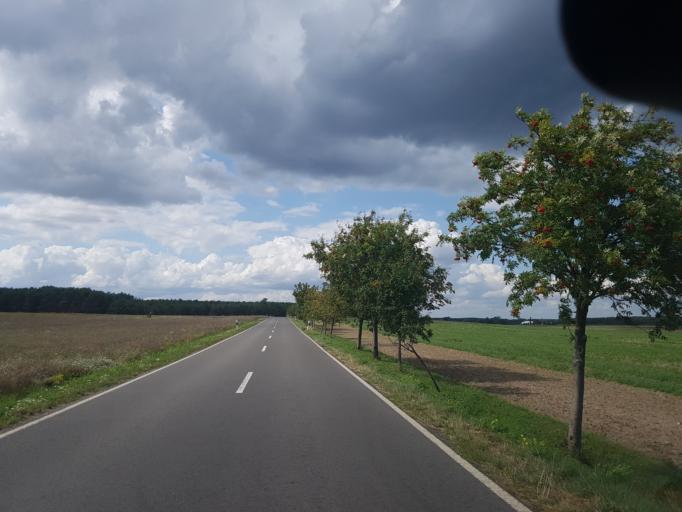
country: DE
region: Brandenburg
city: Schlieben
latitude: 51.6839
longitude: 13.3469
